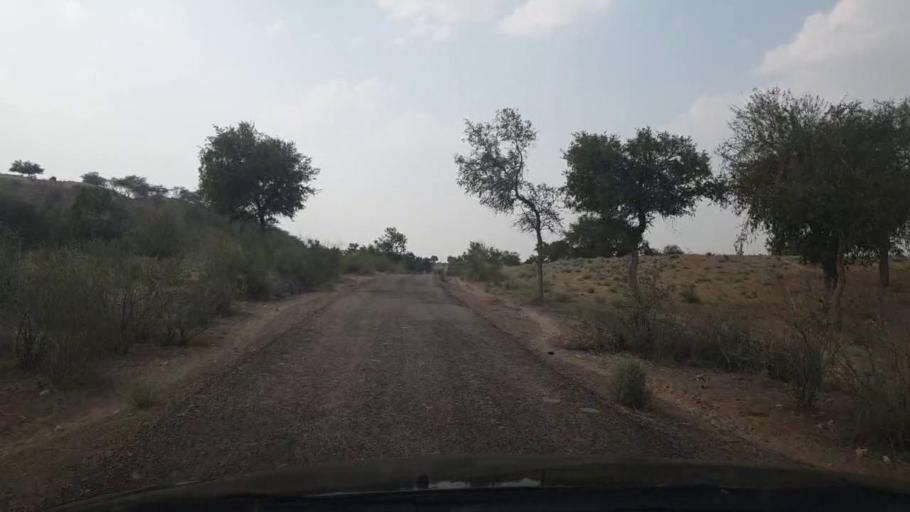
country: PK
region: Sindh
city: Islamkot
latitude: 24.9661
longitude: 70.6033
